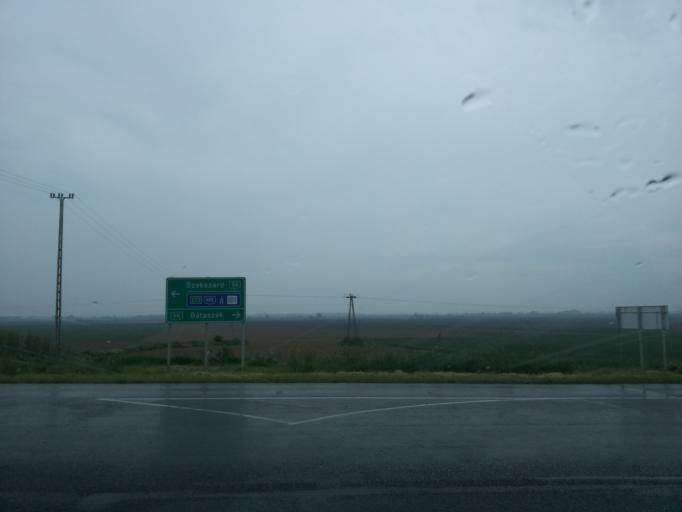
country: HU
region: Tolna
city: Szekszard
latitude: 46.2946
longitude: 18.6857
